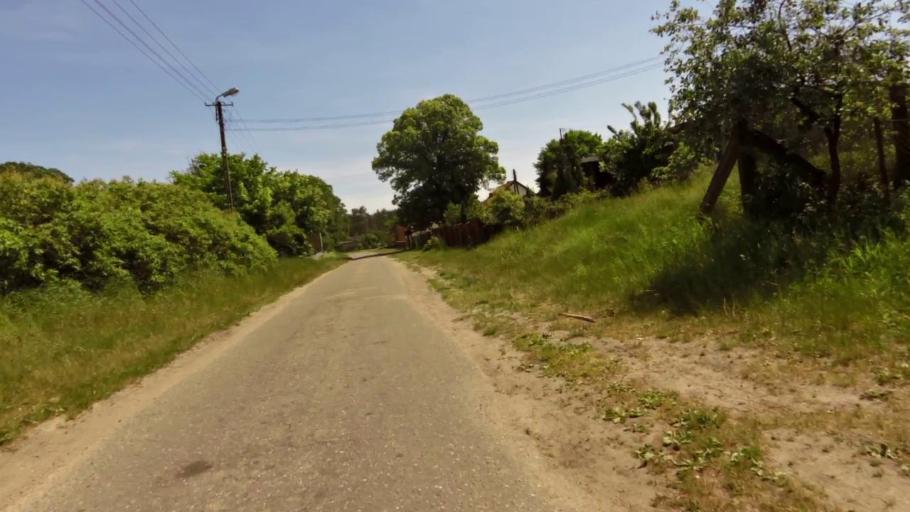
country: PL
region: West Pomeranian Voivodeship
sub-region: Powiat szczecinecki
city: Szczecinek
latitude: 53.6299
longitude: 16.6813
